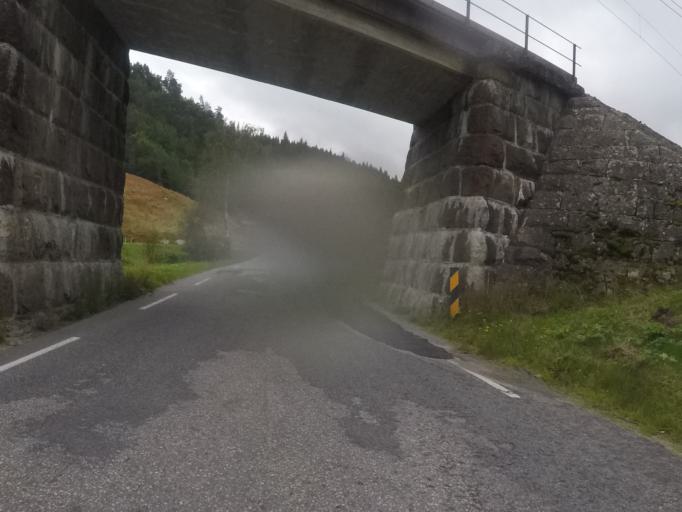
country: NO
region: Vest-Agder
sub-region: Audnedal
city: Konsmo
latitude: 58.2771
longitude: 7.3974
